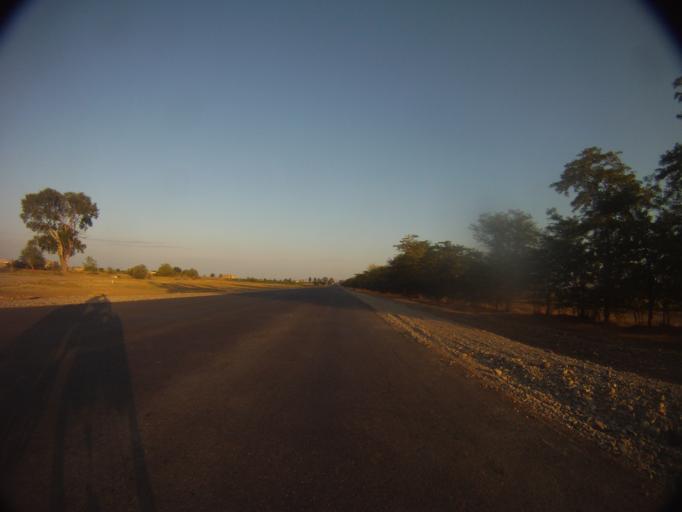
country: GE
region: Kvemo Kartli
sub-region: Gardabani
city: Gardabani
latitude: 41.4147
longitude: 45.0189
